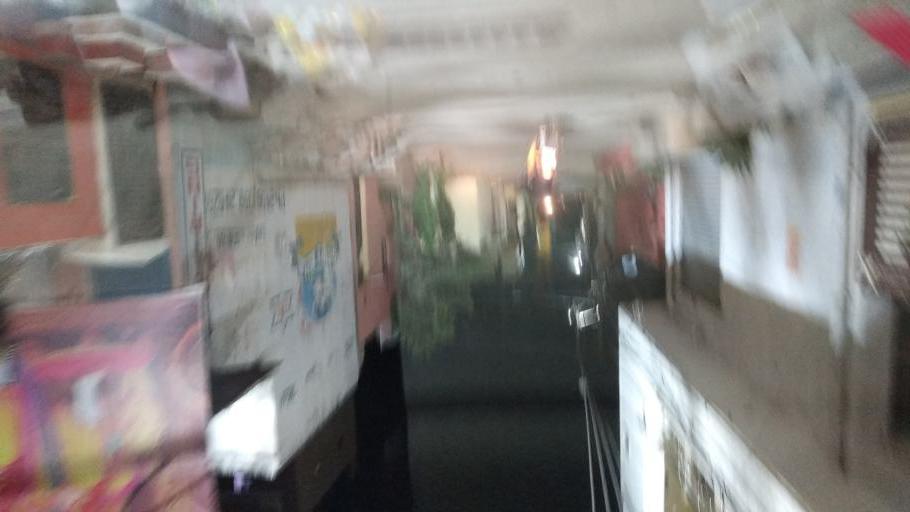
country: IN
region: Telangana
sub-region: Rangareddi
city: Kukatpalli
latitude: 17.4556
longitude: 78.4139
